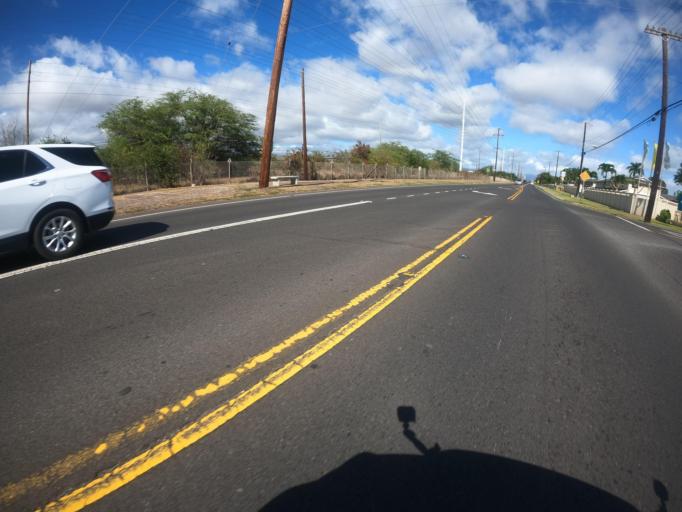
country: US
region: Hawaii
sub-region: Honolulu County
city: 'Ewa Villages
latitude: 21.3260
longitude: -158.0639
